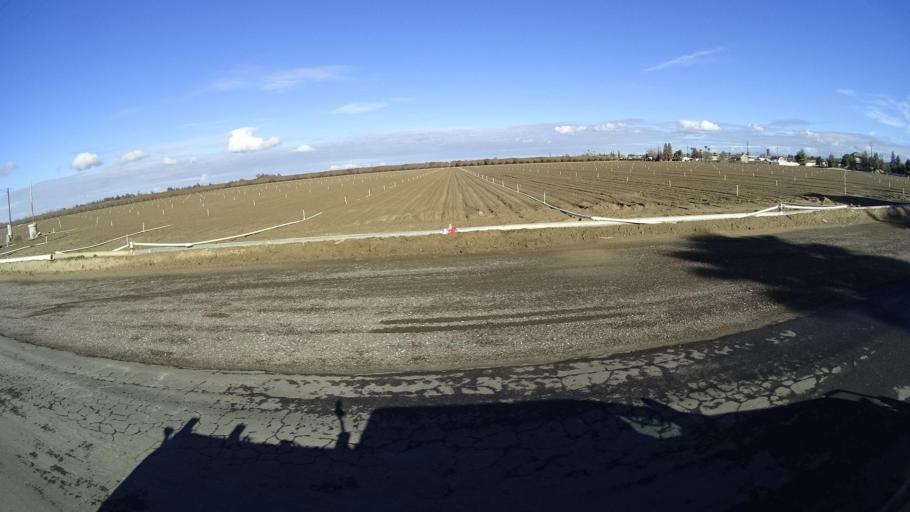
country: US
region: California
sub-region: Kern County
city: Rosedale
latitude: 35.3687
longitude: -119.2011
